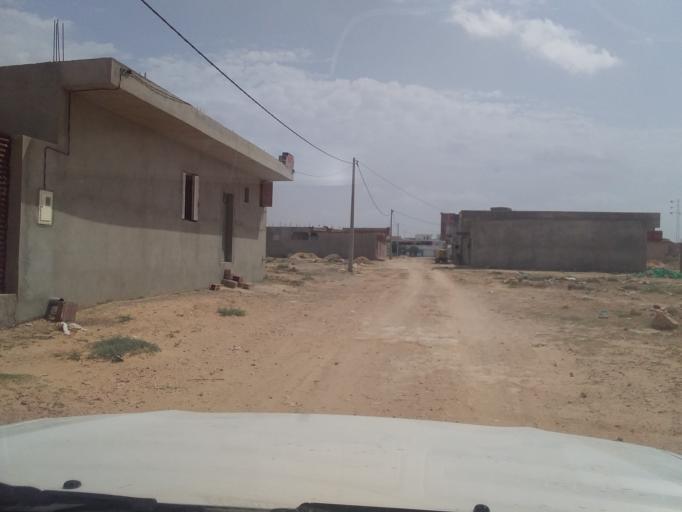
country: TN
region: Qabis
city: Matmata
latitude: 33.6213
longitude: 10.2713
